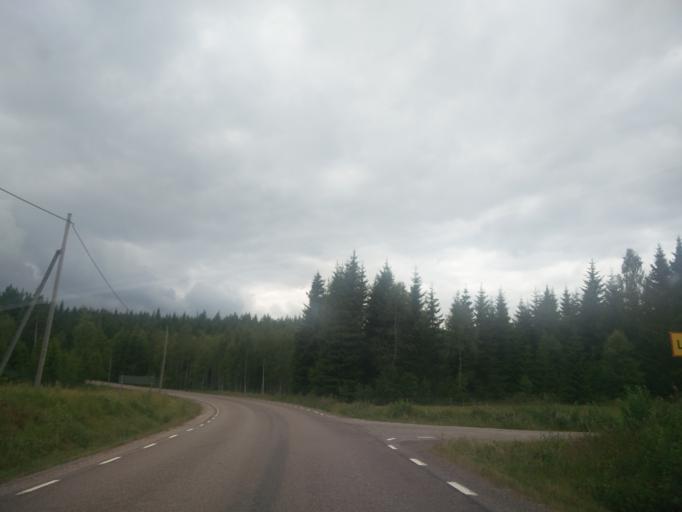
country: SE
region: Vaermland
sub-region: Arvika Kommun
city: Arvika
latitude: 59.9518
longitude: 12.7018
